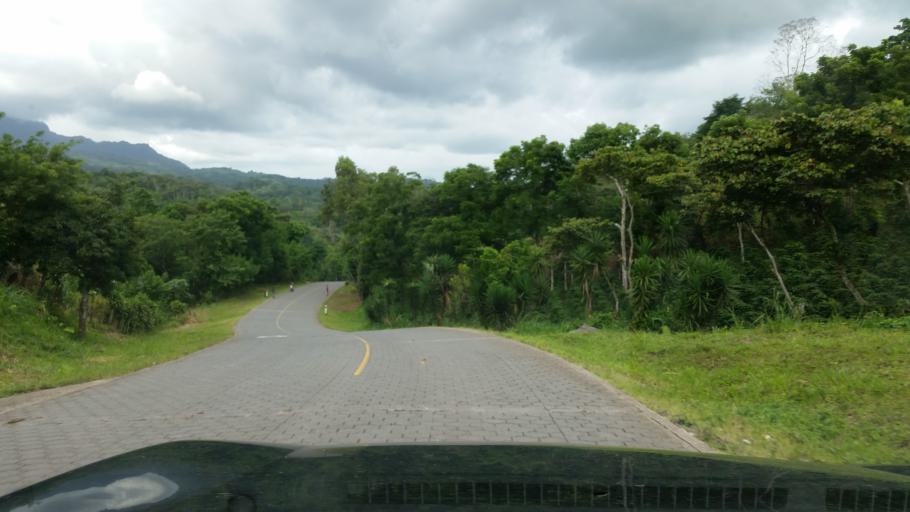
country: NI
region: Jinotega
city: Jinotega
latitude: 13.2038
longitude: -85.7279
